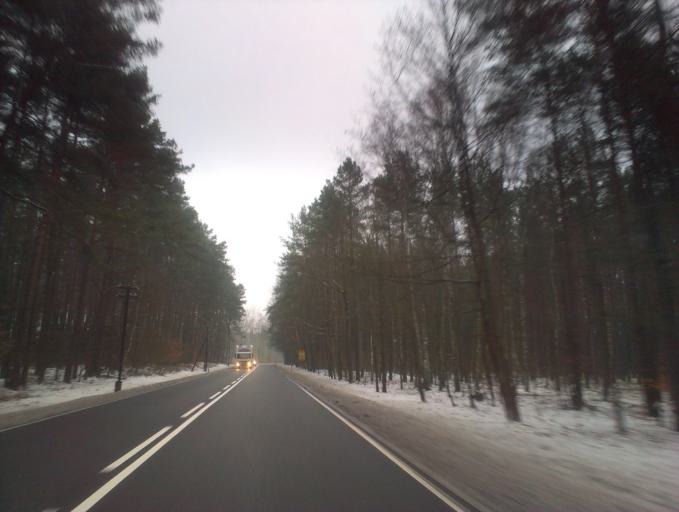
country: PL
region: Greater Poland Voivodeship
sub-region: Powiat zlotowski
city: Tarnowka
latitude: 53.2918
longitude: 16.7822
